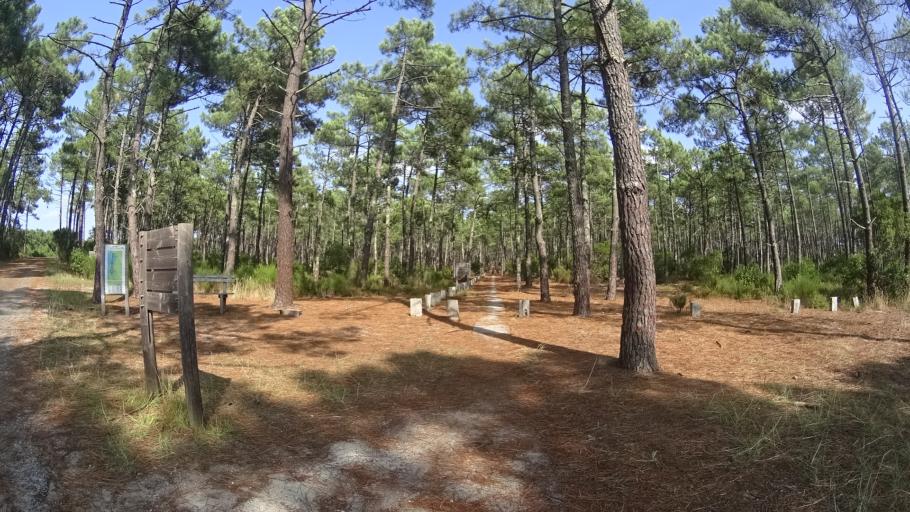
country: FR
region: Aquitaine
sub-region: Departement de la Gironde
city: Lacanau
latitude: 44.9633
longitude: -1.2010
